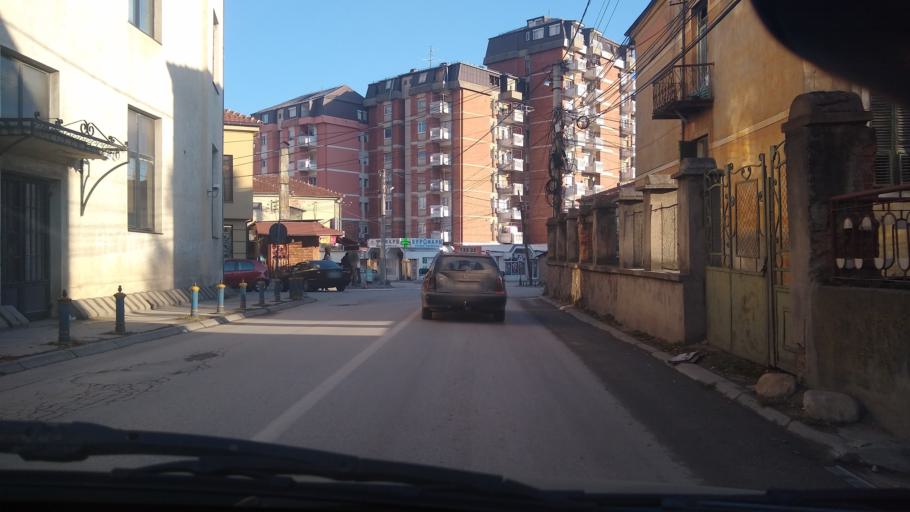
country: MK
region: Bitola
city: Bitola
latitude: 41.0296
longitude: 21.3366
